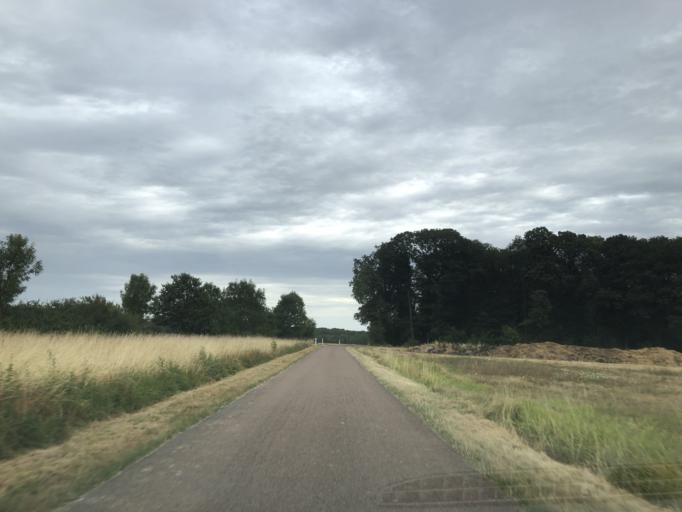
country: FR
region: Bourgogne
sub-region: Departement de l'Yonne
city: Aillant-sur-Tholon
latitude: 47.9014
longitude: 3.3023
